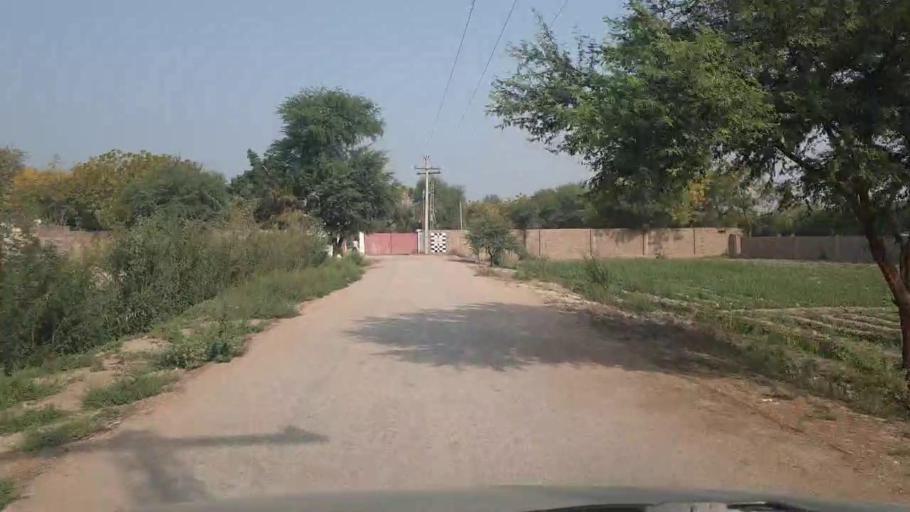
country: PK
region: Sindh
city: Umarkot
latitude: 25.3755
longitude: 69.7374
